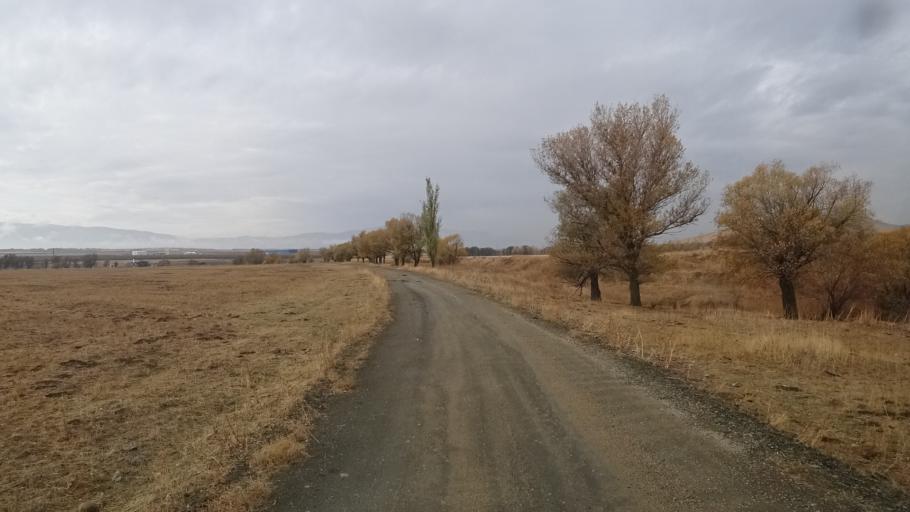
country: KZ
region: Ongtustik Qazaqstan
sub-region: Tulkibas Audany
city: Zhabagly
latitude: 42.5199
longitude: 70.5127
